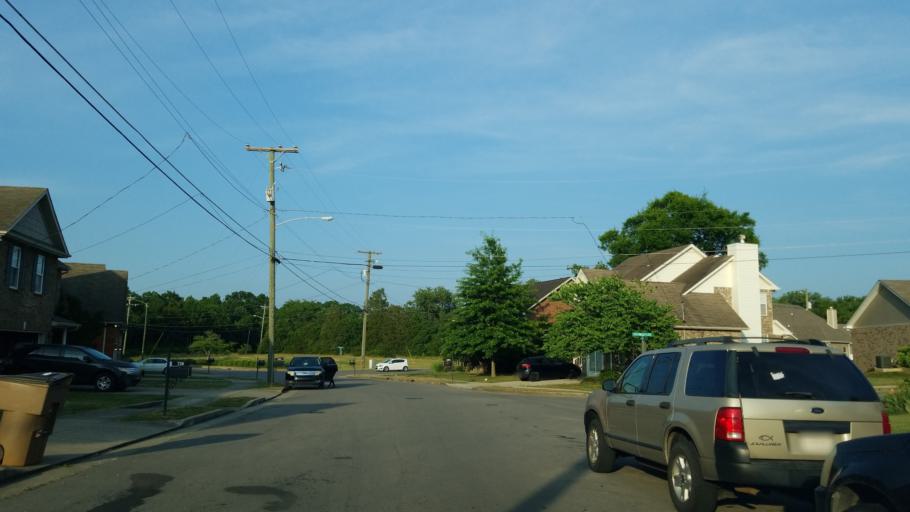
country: US
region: Tennessee
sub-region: Rutherford County
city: La Vergne
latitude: 36.0552
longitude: -86.5890
